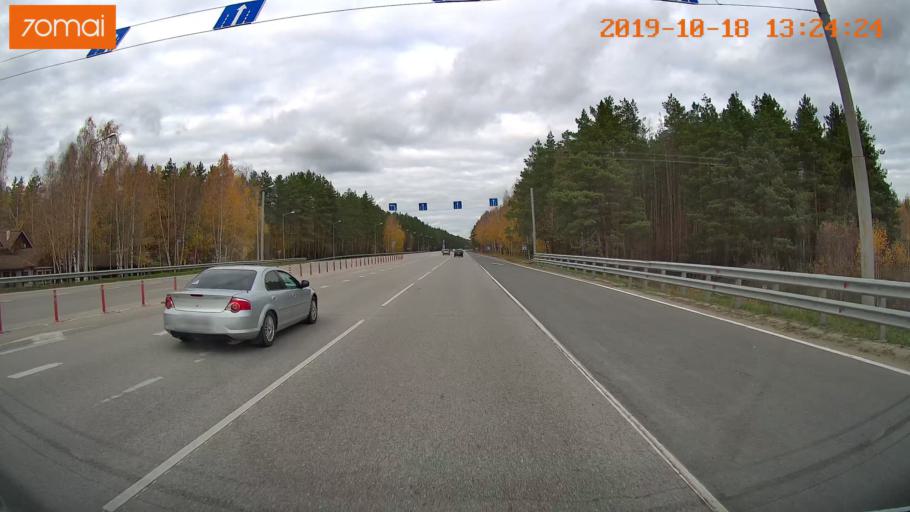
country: RU
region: Rjazan
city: Polyany
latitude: 54.7302
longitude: 39.8442
